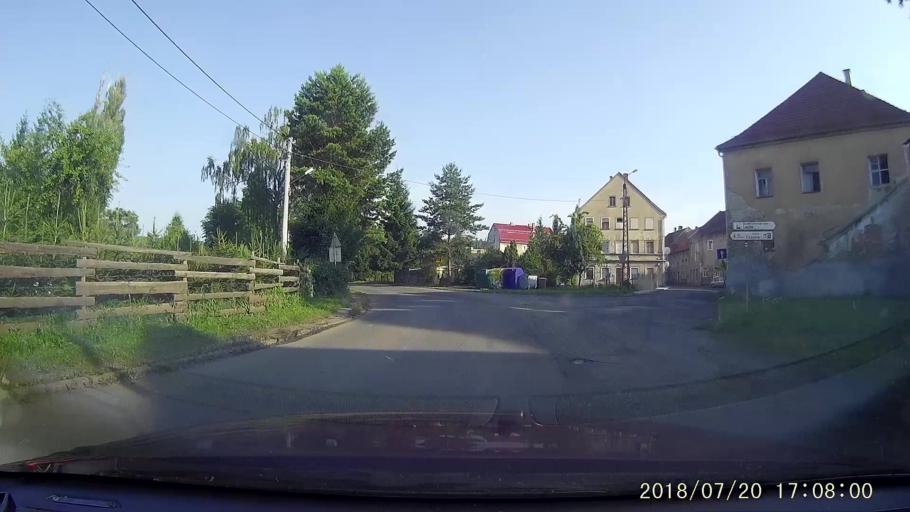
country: PL
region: Lower Silesian Voivodeship
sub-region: Powiat lubanski
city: Lesna
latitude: 51.0256
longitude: 15.2614
